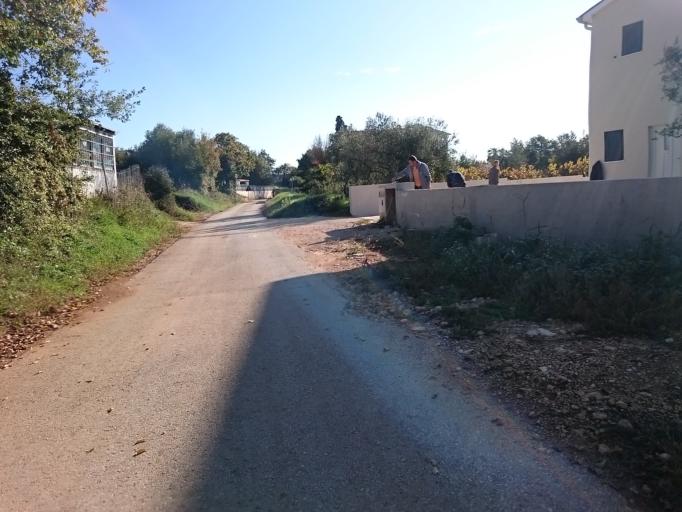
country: HR
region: Istarska
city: Novigrad
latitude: 45.2939
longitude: 13.6096
